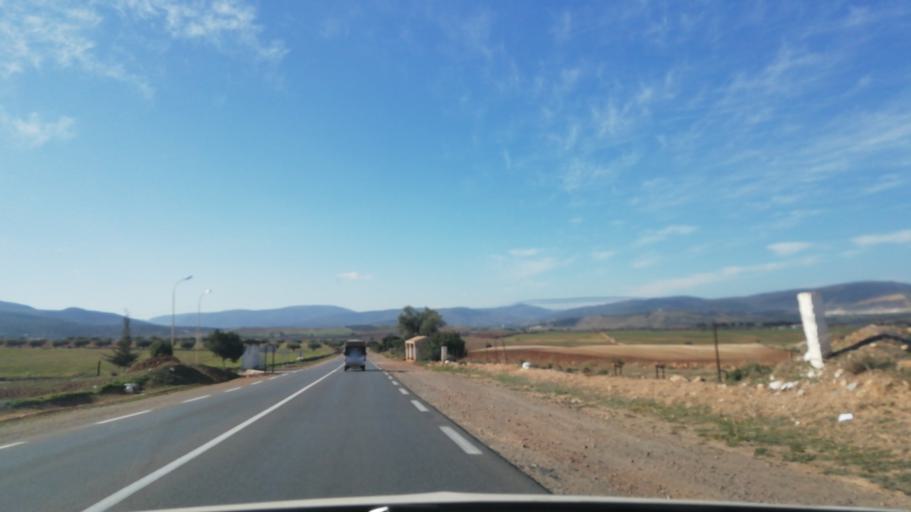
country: DZ
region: Tlemcen
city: Ouled Mimoun
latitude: 34.8813
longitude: -1.0900
